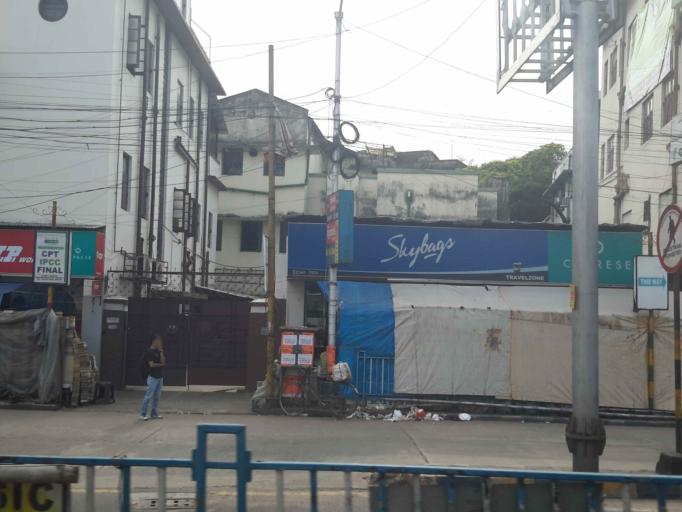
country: IN
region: West Bengal
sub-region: Kolkata
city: Kolkata
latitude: 22.5172
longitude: 88.3661
